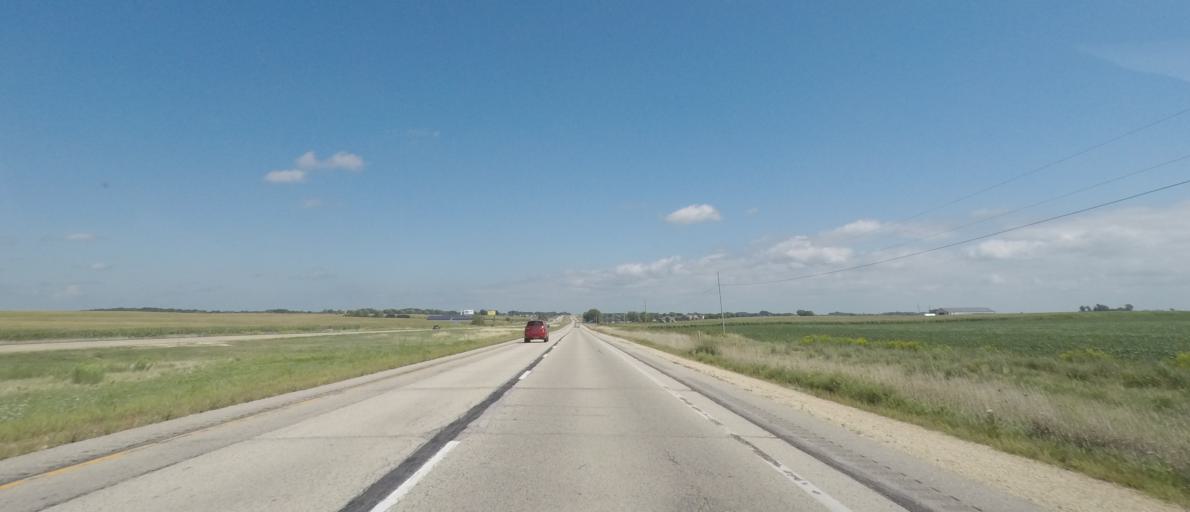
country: US
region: Iowa
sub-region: Jones County
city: Anamosa
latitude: 42.0707
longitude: -91.3581
